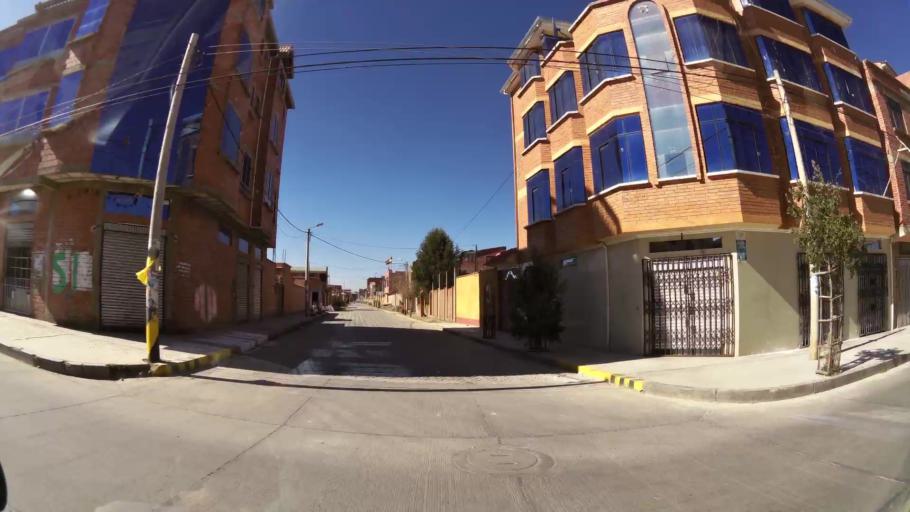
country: BO
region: La Paz
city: La Paz
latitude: -16.5285
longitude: -68.2065
